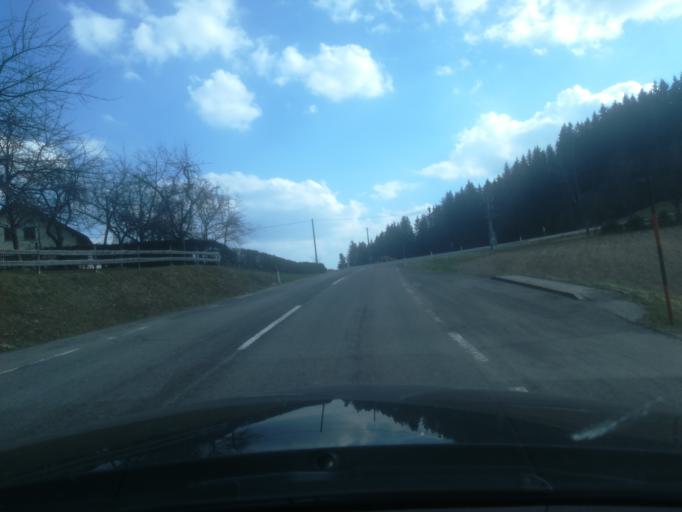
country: AT
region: Lower Austria
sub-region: Politischer Bezirk Zwettl
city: Langschlag
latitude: 48.4597
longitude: 14.7122
